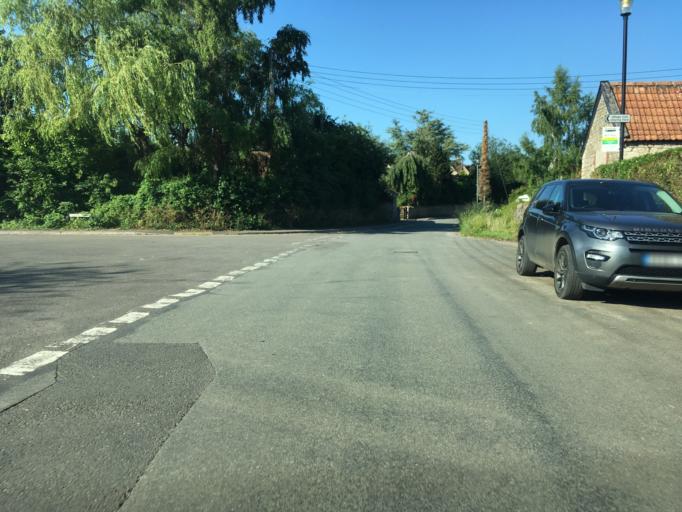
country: GB
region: England
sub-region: South Gloucestershire
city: Hinton
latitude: 51.4648
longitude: -2.4038
